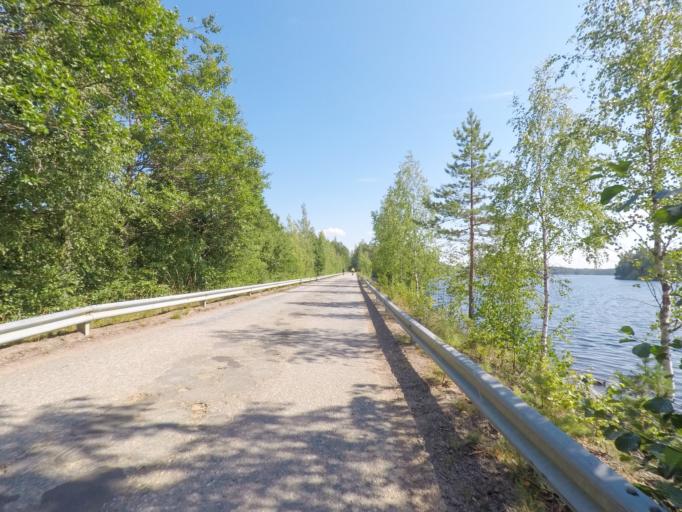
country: FI
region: Southern Savonia
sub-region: Mikkeli
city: Puumala
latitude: 61.4063
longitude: 28.0632
